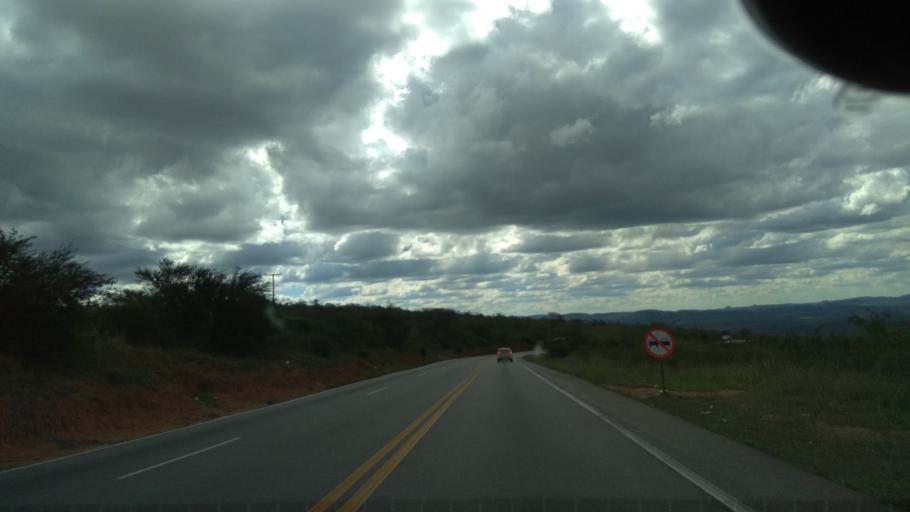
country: BR
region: Bahia
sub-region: Santa Ines
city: Santa Ines
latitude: -13.0545
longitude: -39.9593
